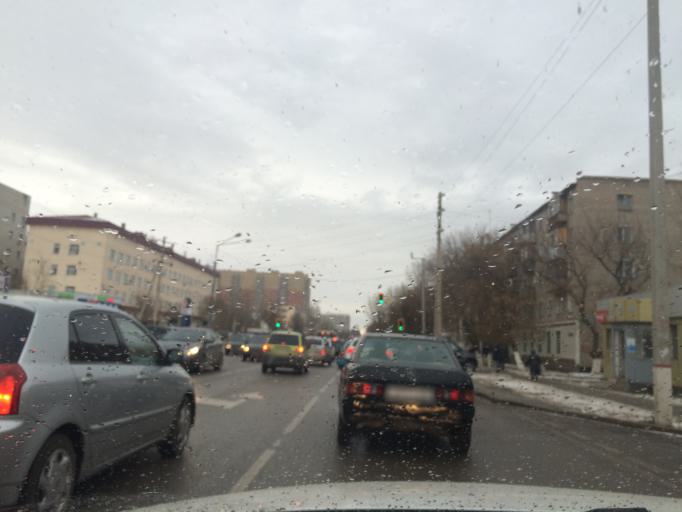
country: KZ
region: Astana Qalasy
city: Astana
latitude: 51.1817
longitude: 71.4226
